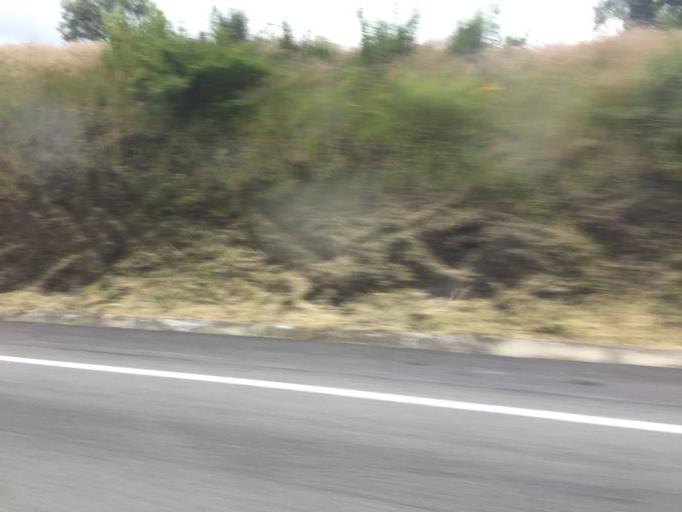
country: MX
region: Jalisco
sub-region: Zapotlan del Rey
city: Zapotlan del Rey
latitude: 20.5109
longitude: -102.9701
